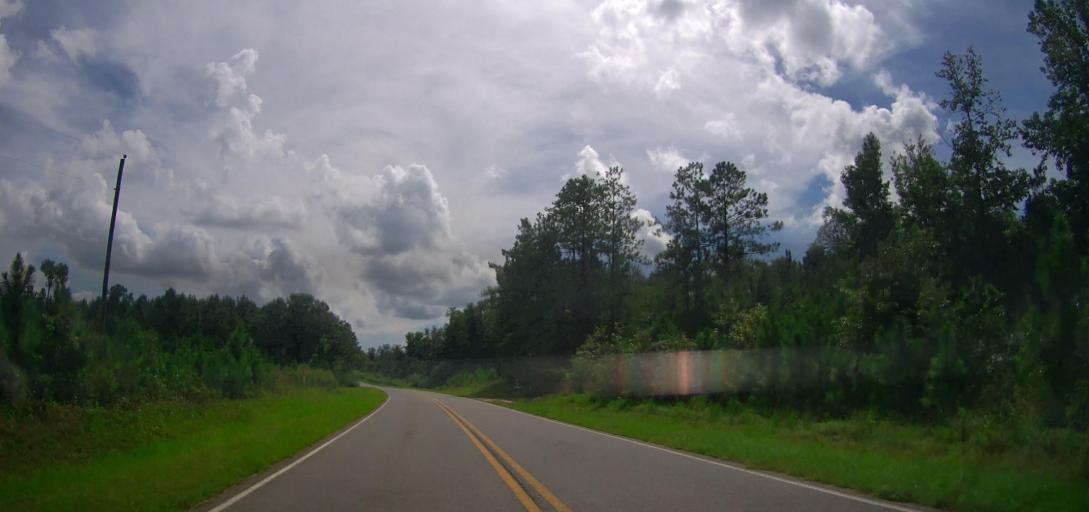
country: US
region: Georgia
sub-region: Taylor County
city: Butler
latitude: 32.4947
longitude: -84.2053
